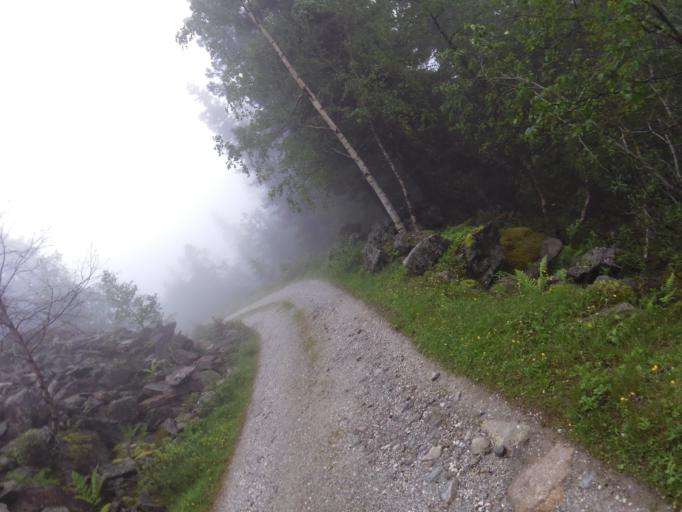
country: AT
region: Tyrol
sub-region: Politischer Bezirk Innsbruck Land
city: Neustift im Stubaital
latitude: 47.0539
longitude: 11.2197
